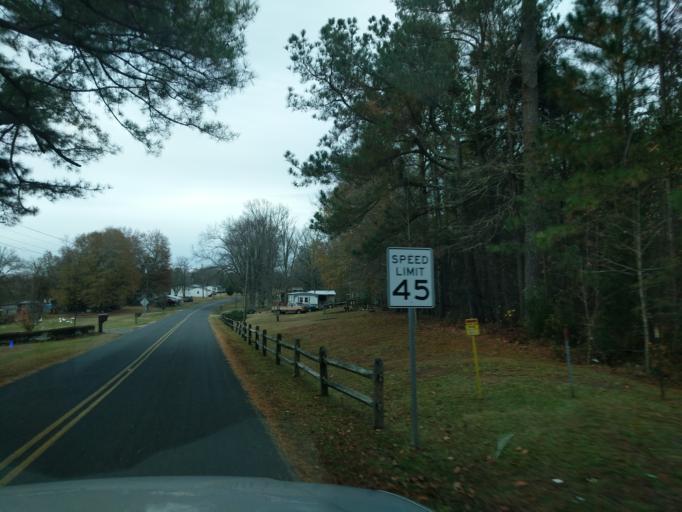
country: US
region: South Carolina
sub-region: Laurens County
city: Clinton
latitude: 34.4079
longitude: -81.9432
